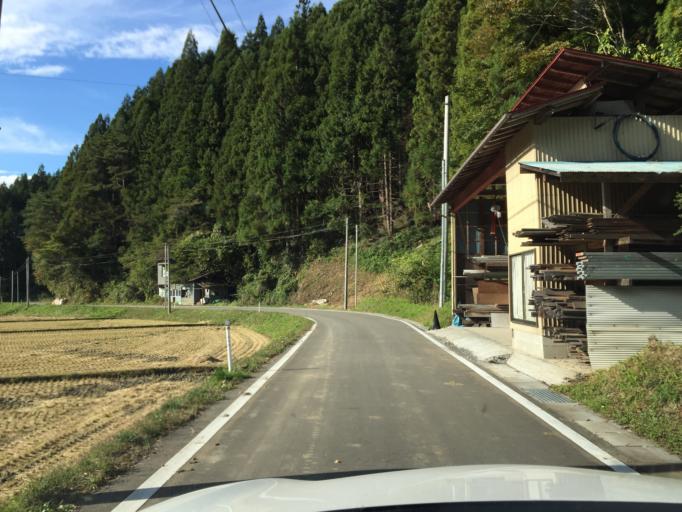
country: JP
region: Fukushima
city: Ishikawa
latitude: 37.1656
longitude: 140.5015
